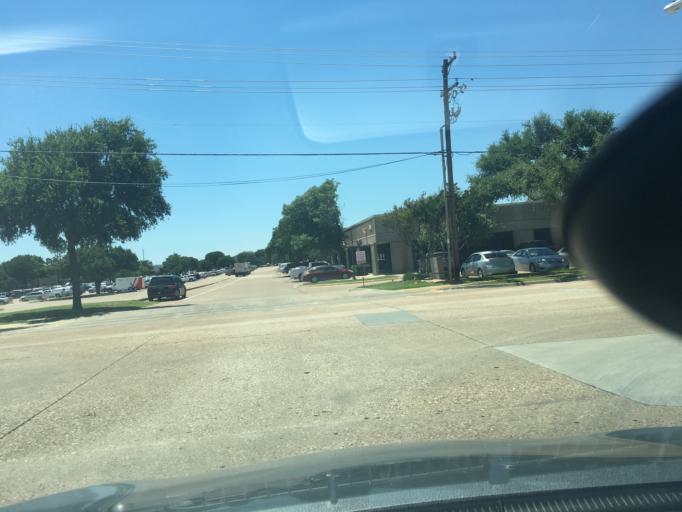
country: US
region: Texas
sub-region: Dallas County
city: Richardson
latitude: 32.9557
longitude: -96.7051
